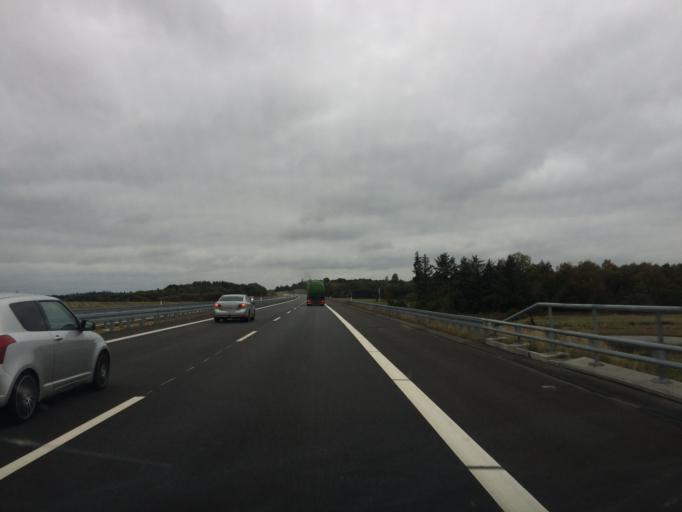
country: DK
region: Central Jutland
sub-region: Silkeborg Kommune
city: Silkeborg
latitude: 56.1870
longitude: 9.4908
